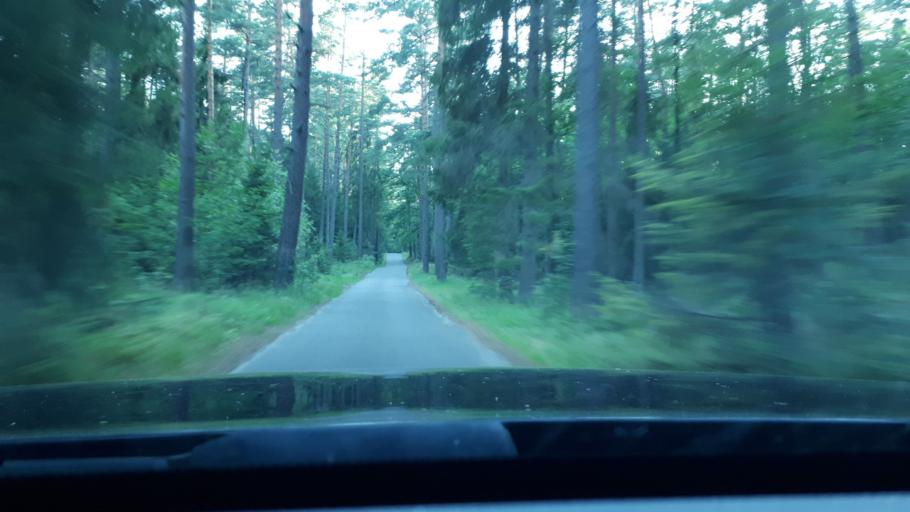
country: PL
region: Warmian-Masurian Voivodeship
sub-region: Powiat olsztynski
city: Stawiguda
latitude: 53.5884
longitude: 20.4537
